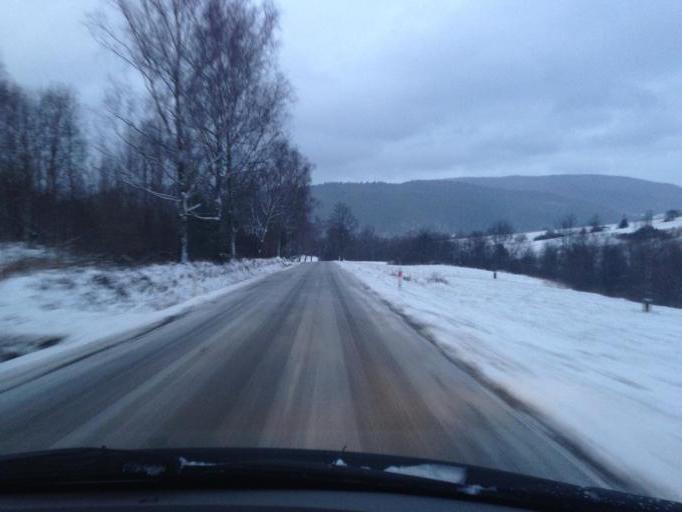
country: PL
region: Subcarpathian Voivodeship
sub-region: Powiat jasielski
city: Krempna
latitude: 49.5211
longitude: 21.5023
